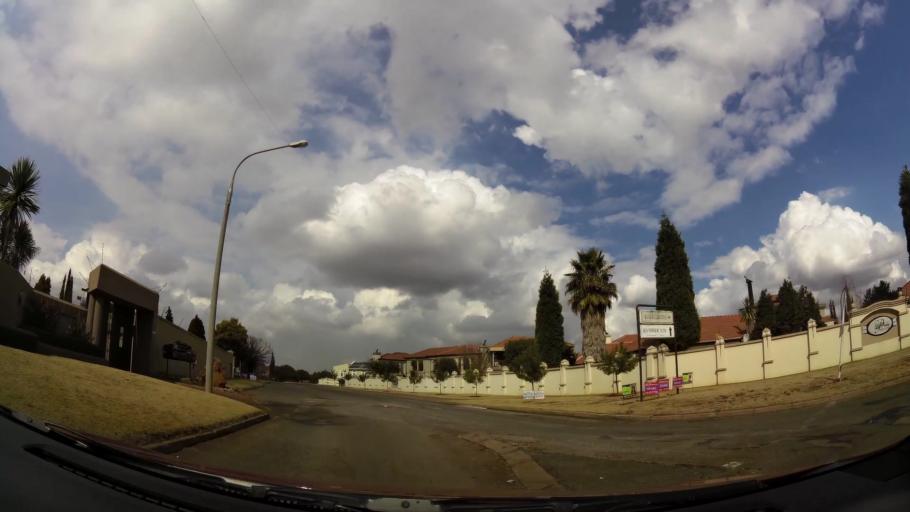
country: ZA
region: Gauteng
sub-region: Sedibeng District Municipality
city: Vanderbijlpark
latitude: -26.7459
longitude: 27.8285
